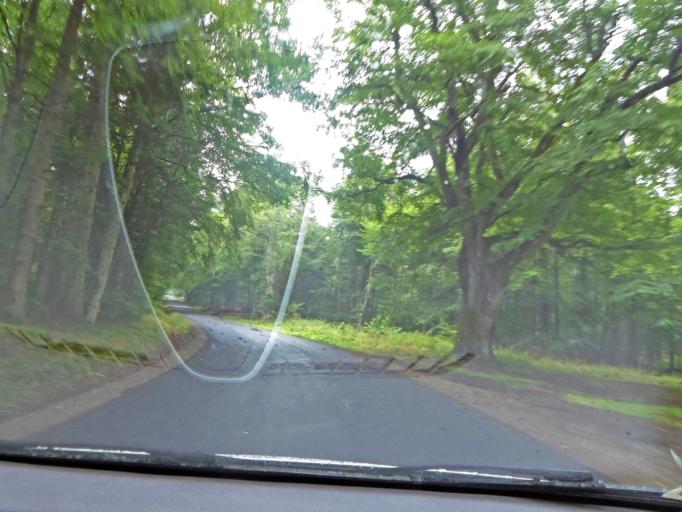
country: FR
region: Auvergne
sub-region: Departement du Puy-de-Dome
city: Orcines
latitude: 45.7452
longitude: 2.9393
